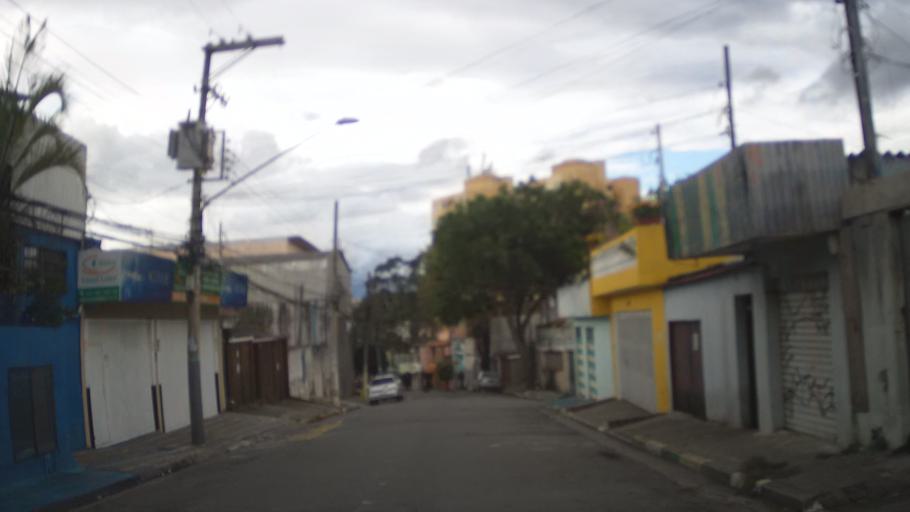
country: BR
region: Sao Paulo
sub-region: Guarulhos
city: Guarulhos
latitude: -23.4776
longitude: -46.5516
